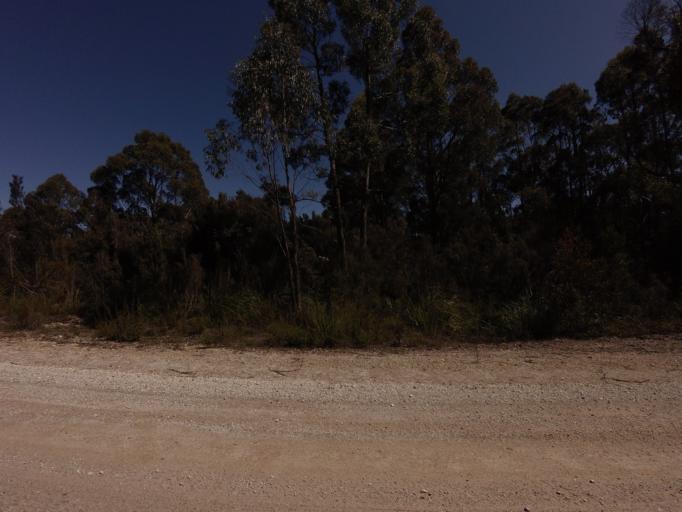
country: AU
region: Tasmania
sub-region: Huon Valley
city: Geeveston
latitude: -42.9090
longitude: 146.3643
